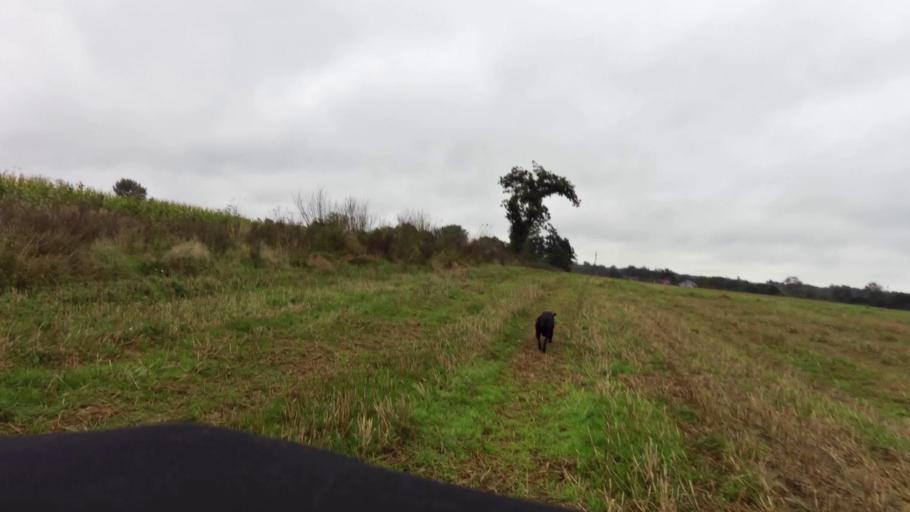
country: PL
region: West Pomeranian Voivodeship
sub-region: Powiat stargardzki
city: Dobrzany
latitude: 53.3817
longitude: 15.4279
